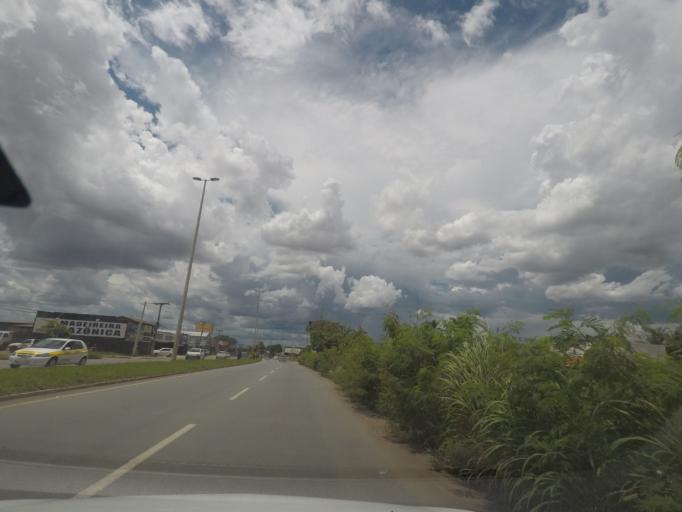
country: BR
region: Goias
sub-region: Goiania
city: Goiania
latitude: -16.7508
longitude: -49.3340
